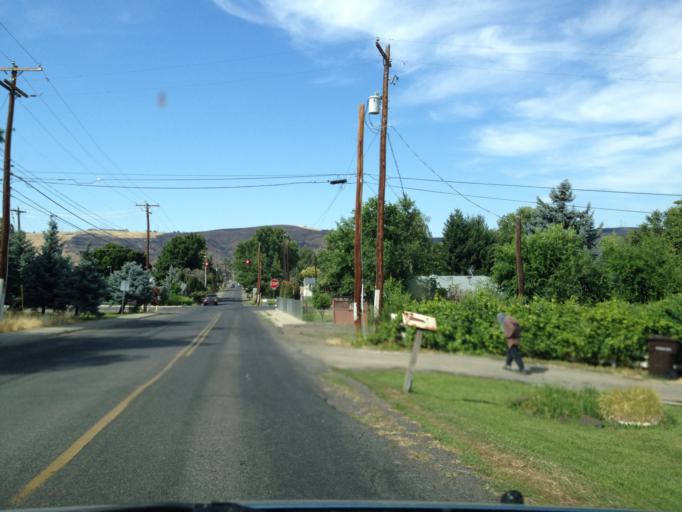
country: US
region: Washington
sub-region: Yakima County
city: Yakima
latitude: 46.6093
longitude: -120.5541
